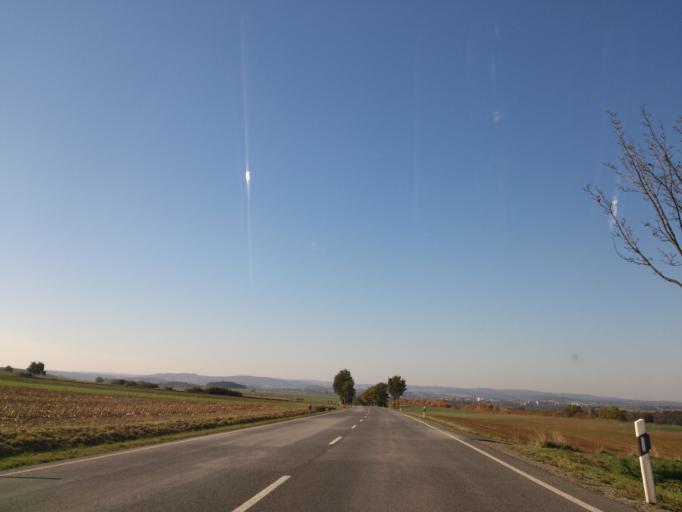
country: DE
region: Hesse
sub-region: Regierungsbezirk Kassel
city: Breuna
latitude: 51.4600
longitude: 9.2203
